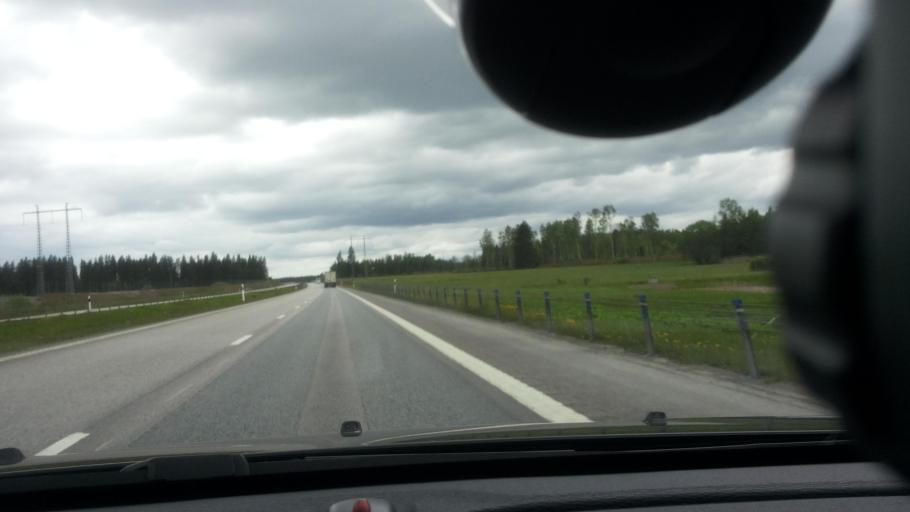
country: SE
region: Uppsala
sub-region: Osthammars Kommun
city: Bjorklinge
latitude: 60.1028
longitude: 17.5633
